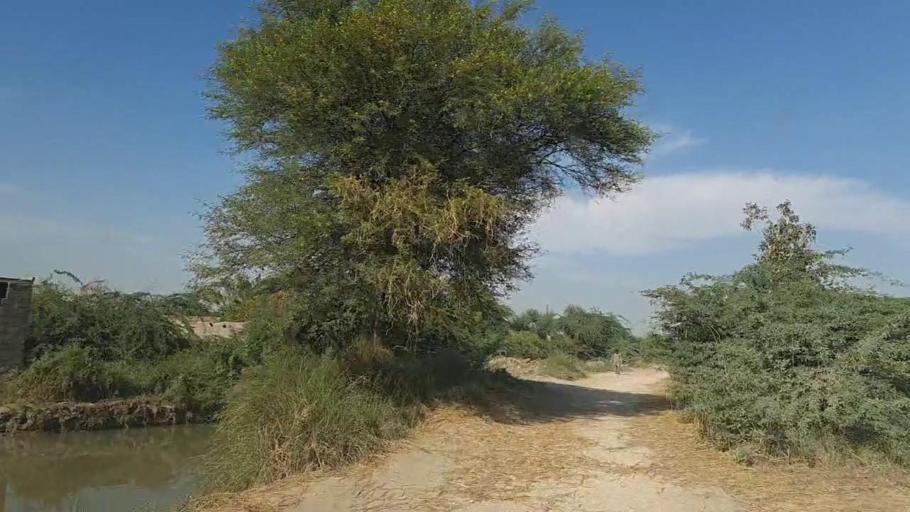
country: PK
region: Sindh
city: Bulri
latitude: 24.8610
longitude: 68.2601
